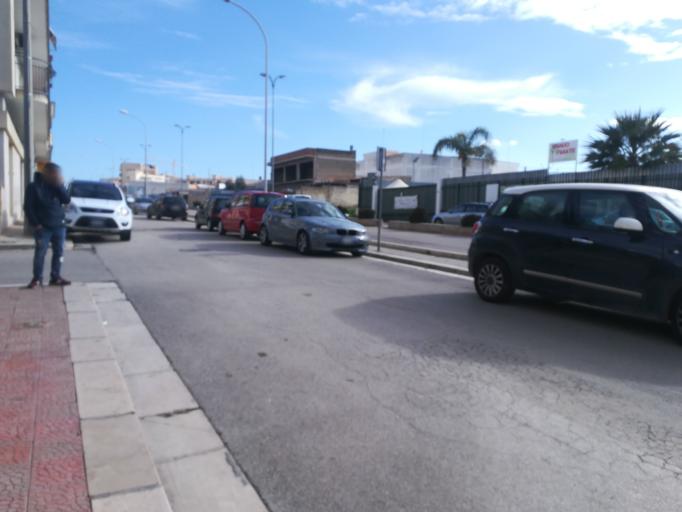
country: IT
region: Apulia
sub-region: Provincia di Barletta - Andria - Trani
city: Andria
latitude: 41.2182
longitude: 16.3008
